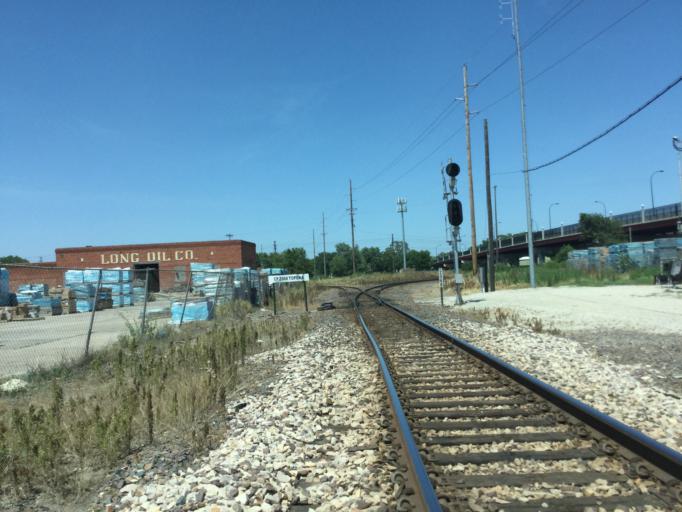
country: US
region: Kansas
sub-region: Shawnee County
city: Topeka
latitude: 39.0662
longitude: -95.6744
